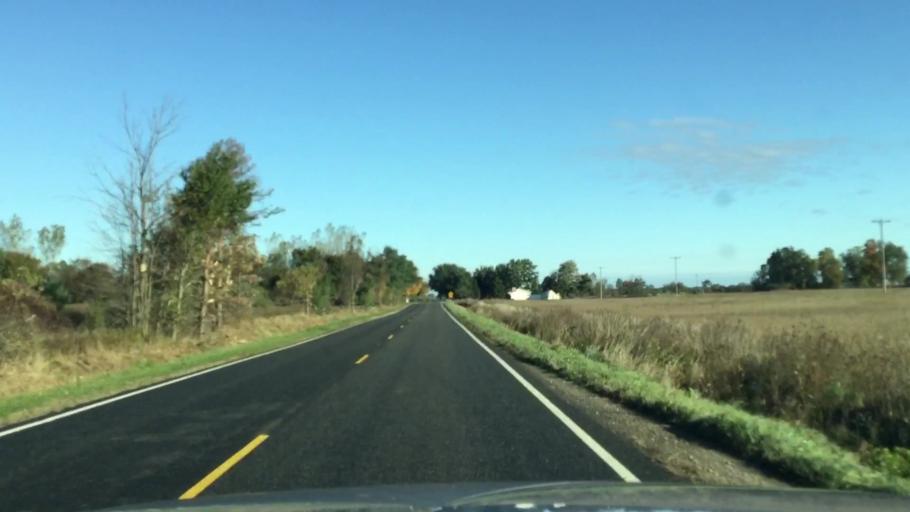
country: US
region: Michigan
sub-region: Shiawassee County
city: Durand
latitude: 42.8793
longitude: -83.9473
